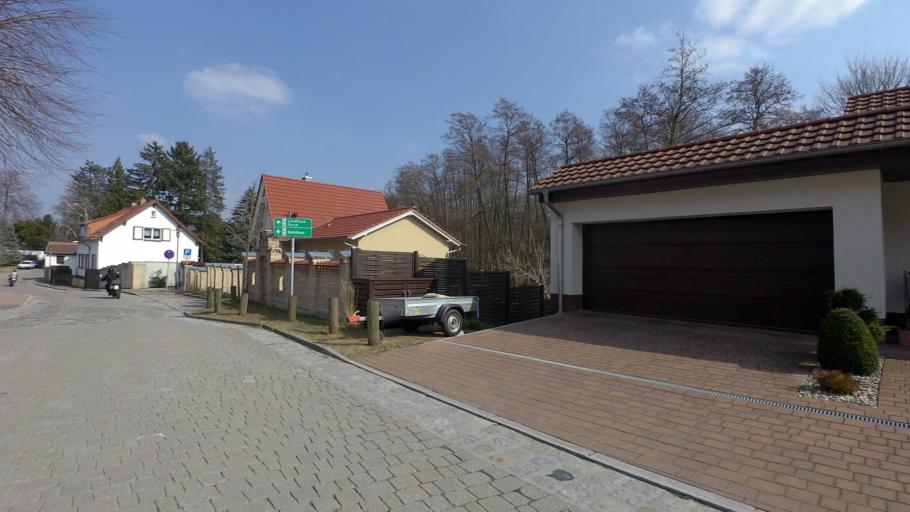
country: DE
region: Brandenburg
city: Fichtenwalde
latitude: 52.3129
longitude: 12.9340
